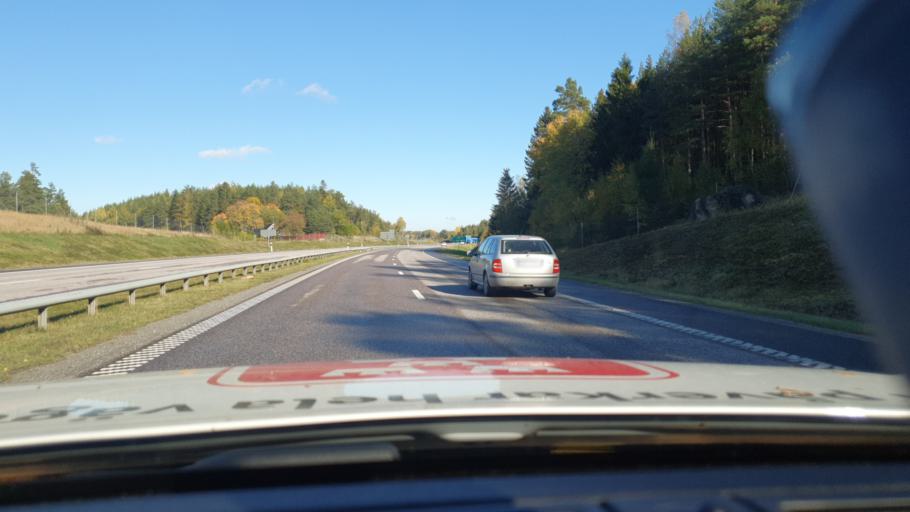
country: SE
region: Stockholm
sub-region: Nynashamns Kommun
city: Osmo
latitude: 58.9844
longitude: 17.9220
